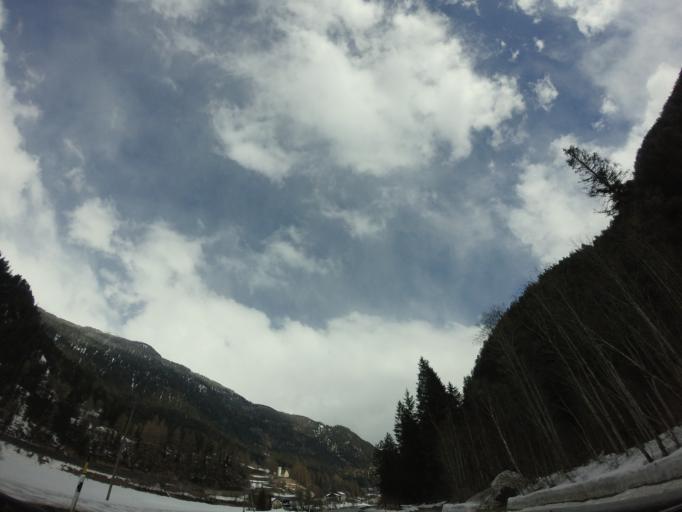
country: AT
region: Tyrol
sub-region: Politischer Bezirk Landeck
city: Nauders
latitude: 46.8770
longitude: 10.4579
